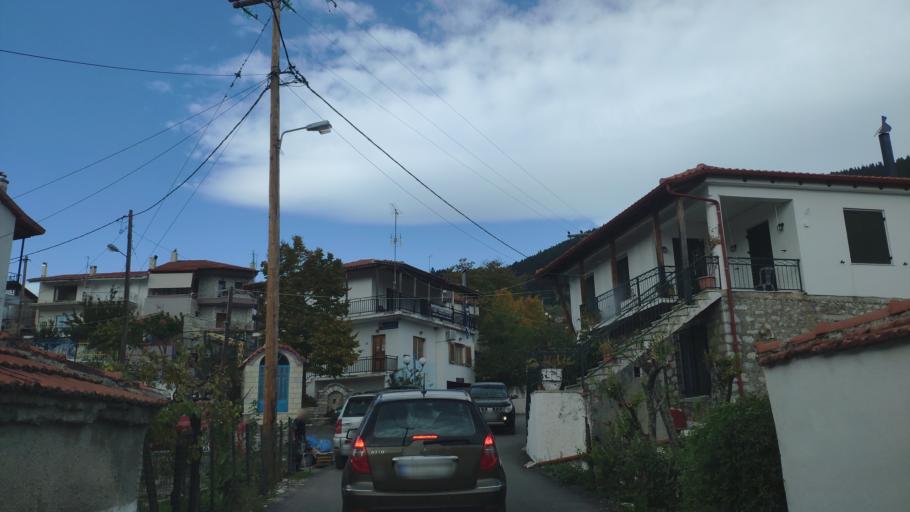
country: GR
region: Central Greece
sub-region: Nomos Fthiotidos
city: Stavros
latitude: 38.7401
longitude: 22.3394
